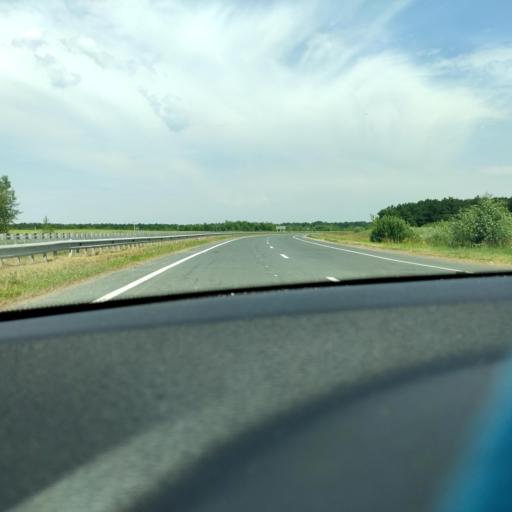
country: RU
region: Samara
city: Petra-Dubrava
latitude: 53.3365
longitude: 50.4313
